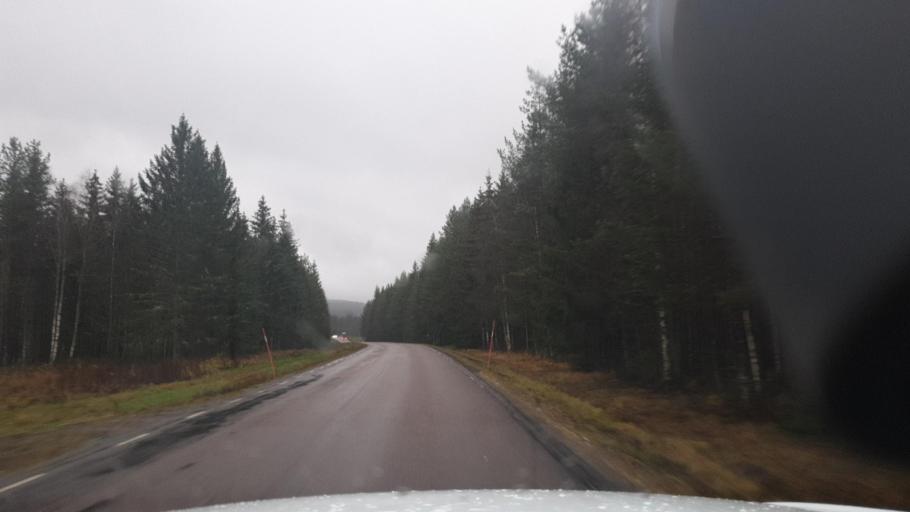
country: SE
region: Vaermland
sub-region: Eda Kommun
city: Charlottenberg
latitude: 59.7369
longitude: 12.1687
